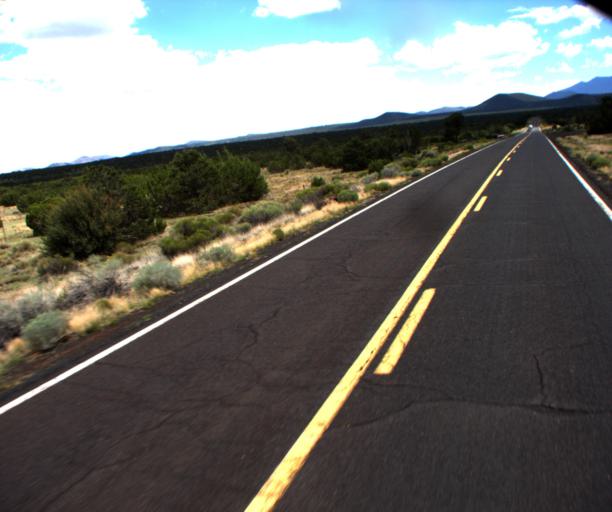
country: US
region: Arizona
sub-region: Coconino County
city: Parks
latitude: 35.5533
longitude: -111.8681
